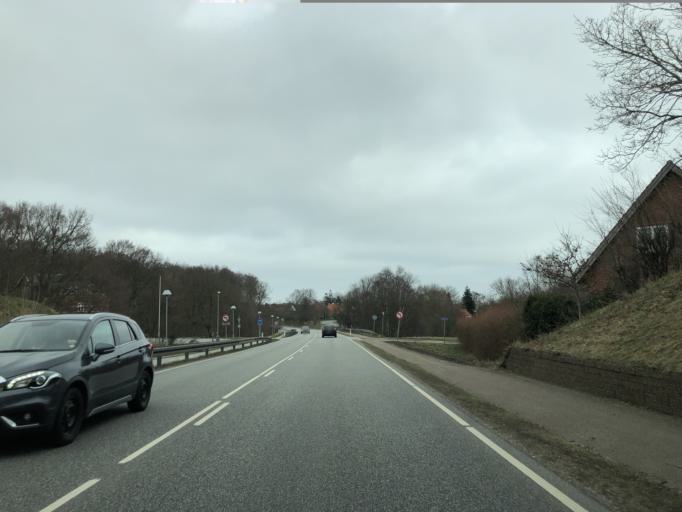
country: DK
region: North Denmark
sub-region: Frederikshavn Kommune
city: Saeby
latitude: 57.3343
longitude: 10.5099
